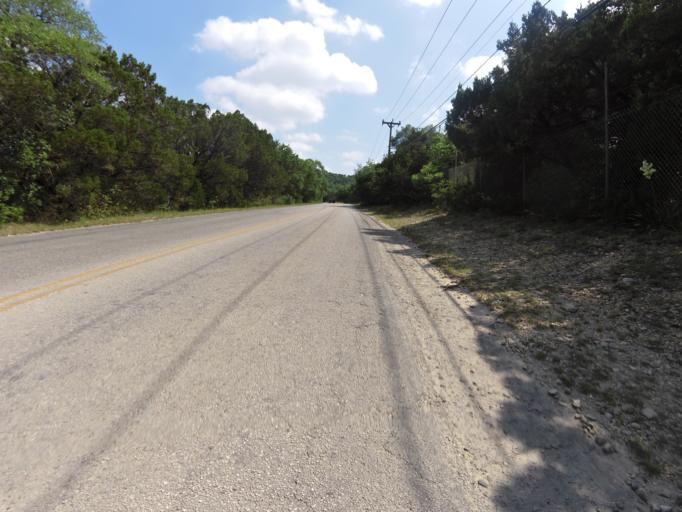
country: US
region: Texas
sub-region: Bexar County
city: Cross Mountain
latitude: 29.6360
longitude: -98.6249
